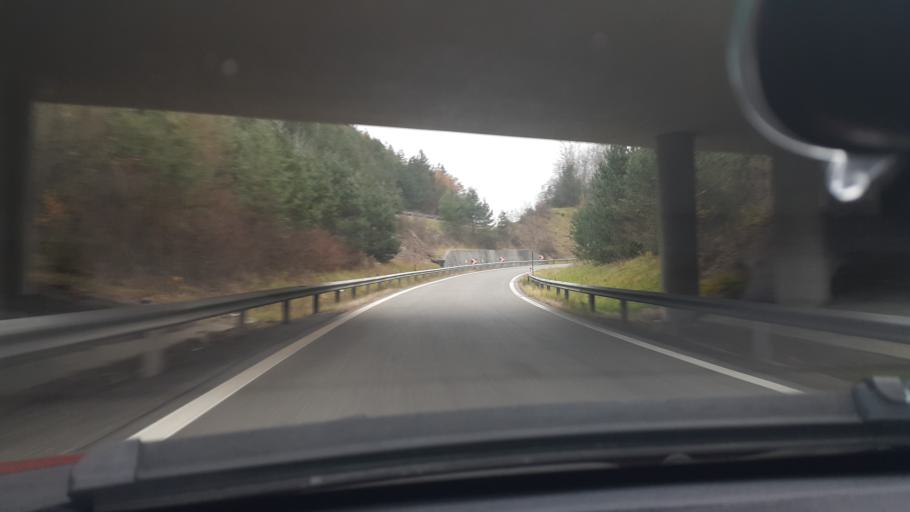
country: AT
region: Carinthia
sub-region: Politischer Bezirk Klagenfurt Land
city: Keutschach am See
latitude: 46.6315
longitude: 14.2406
